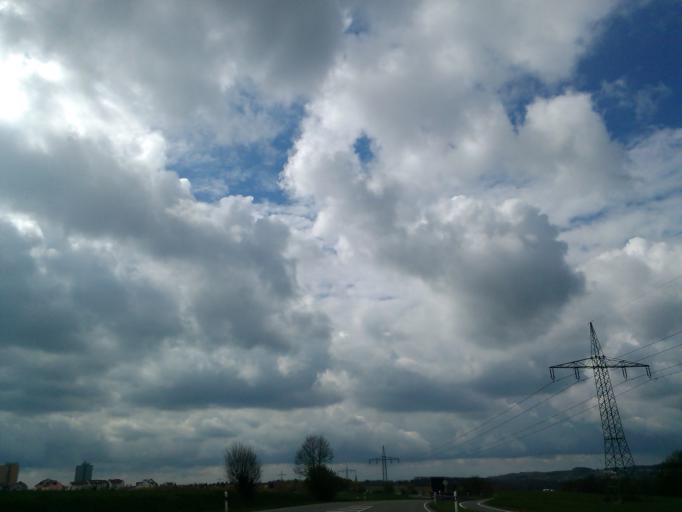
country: DE
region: Bavaria
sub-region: Swabia
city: Neu-Ulm
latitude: 48.4411
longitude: 10.0155
